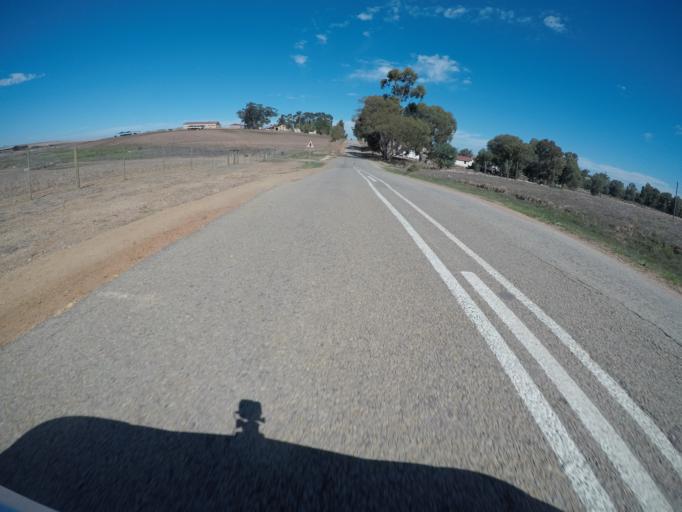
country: ZA
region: Western Cape
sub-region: City of Cape Town
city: Atlantis
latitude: -33.6098
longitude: 18.6376
